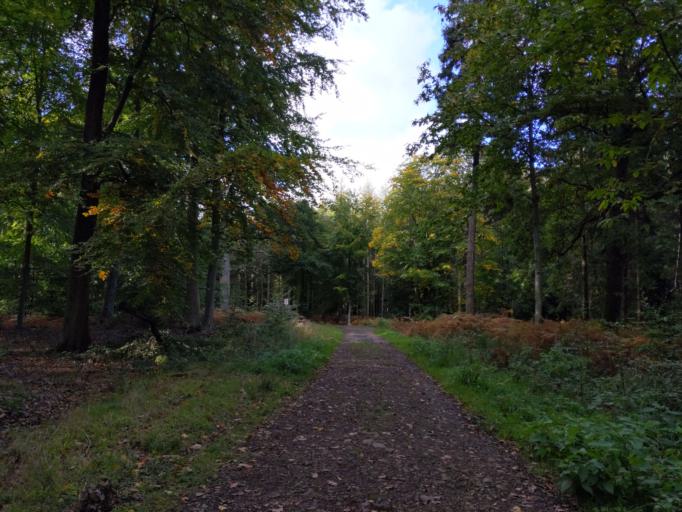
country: GB
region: England
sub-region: Oxfordshire
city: Radley
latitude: 51.7131
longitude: -1.2589
